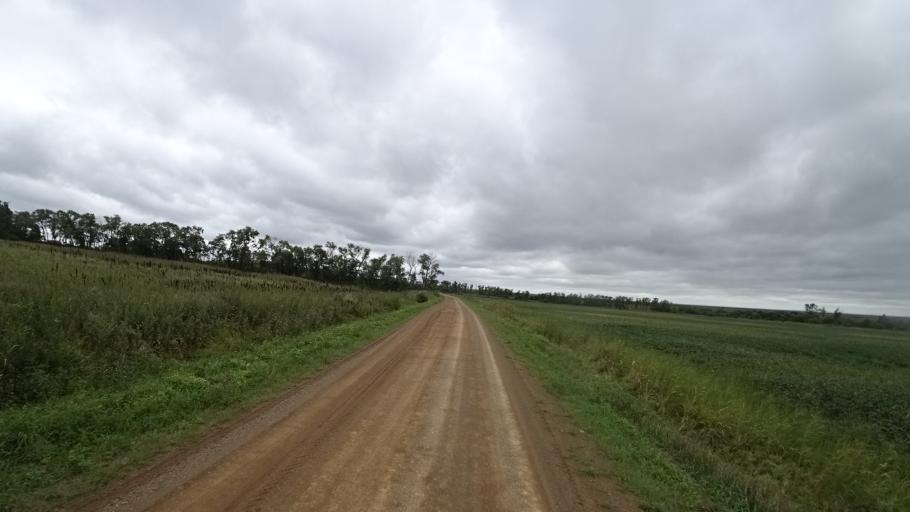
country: RU
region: Primorskiy
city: Chernigovka
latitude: 44.4489
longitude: 132.5759
